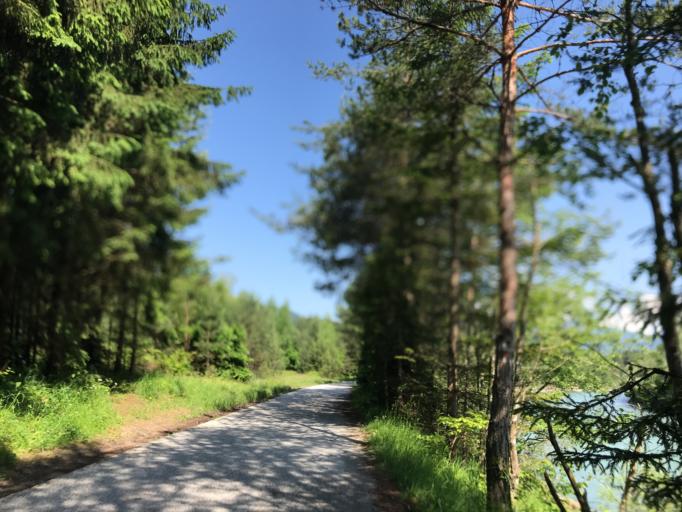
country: AT
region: Carinthia
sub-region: Politischer Bezirk Villach Land
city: Finkenstein am Faaker See
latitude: 46.5770
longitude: 13.8394
